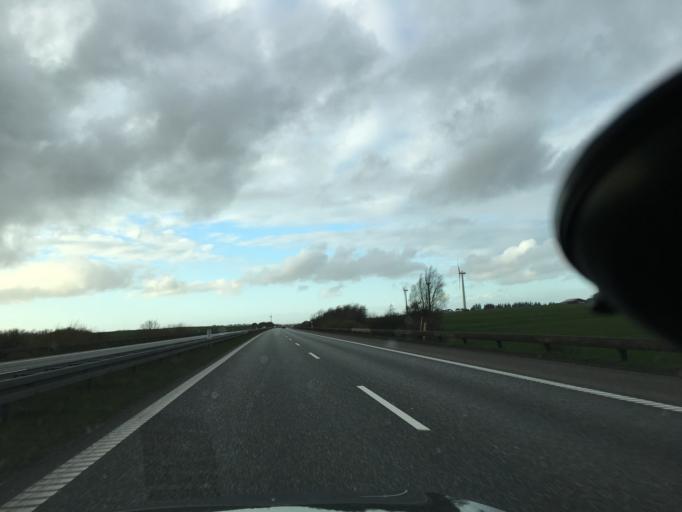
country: DK
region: North Denmark
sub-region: Mariagerfjord Kommune
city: Hobro
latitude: 56.7548
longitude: 9.6950
